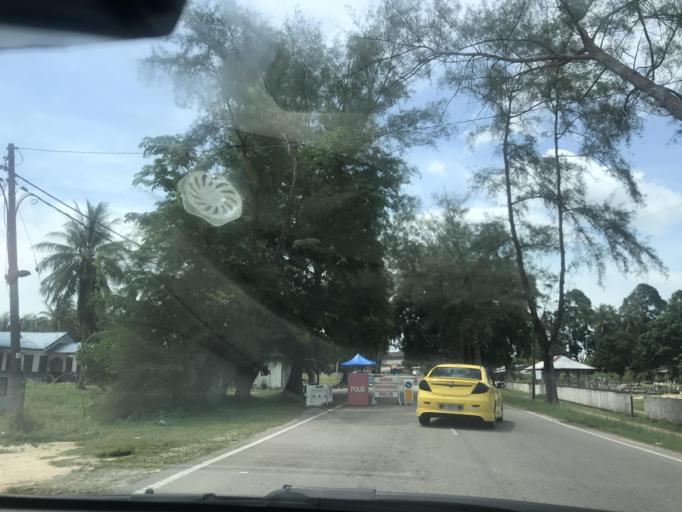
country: MY
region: Kelantan
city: Tumpat
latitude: 6.2116
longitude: 102.1321
